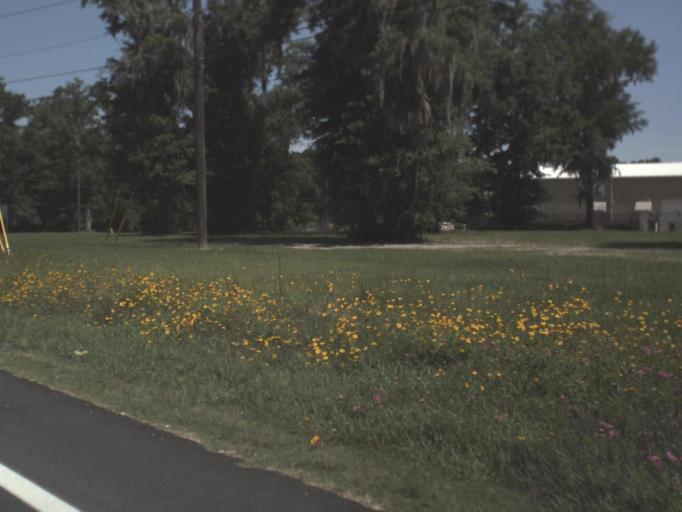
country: US
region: Florida
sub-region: Columbia County
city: Lake City
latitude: 30.1908
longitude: -82.7224
